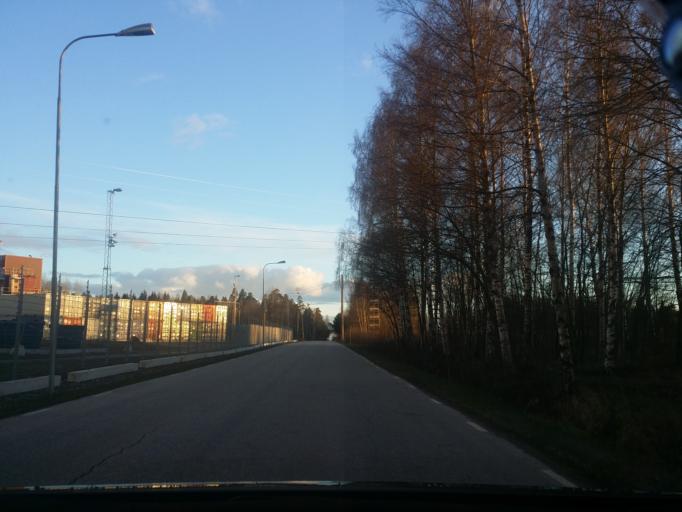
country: SE
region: Vaestmanland
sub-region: Vasteras
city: Hokasen
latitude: 59.6467
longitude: 16.5848
